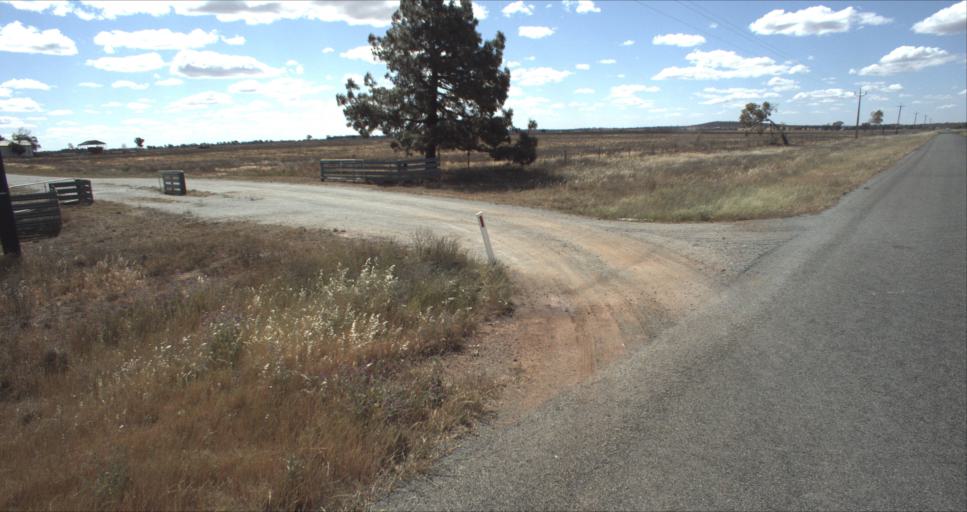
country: AU
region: New South Wales
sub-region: Leeton
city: Leeton
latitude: -34.4572
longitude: 146.2534
